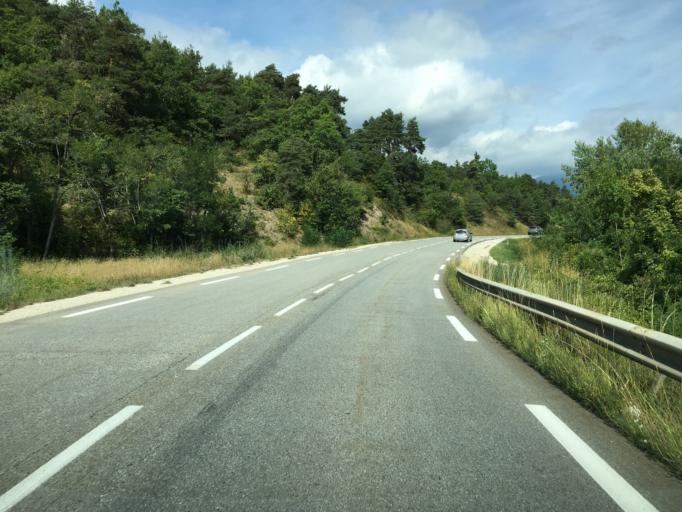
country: FR
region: Rhone-Alpes
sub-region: Departement de l'Isere
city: Mens
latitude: 44.8042
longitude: 5.6302
